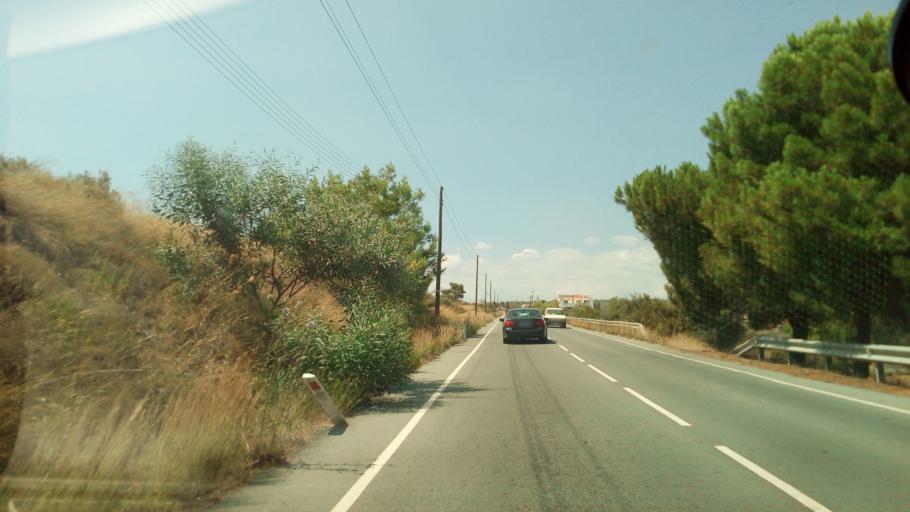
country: CY
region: Limassol
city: Sotira
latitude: 34.7284
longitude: 32.8892
